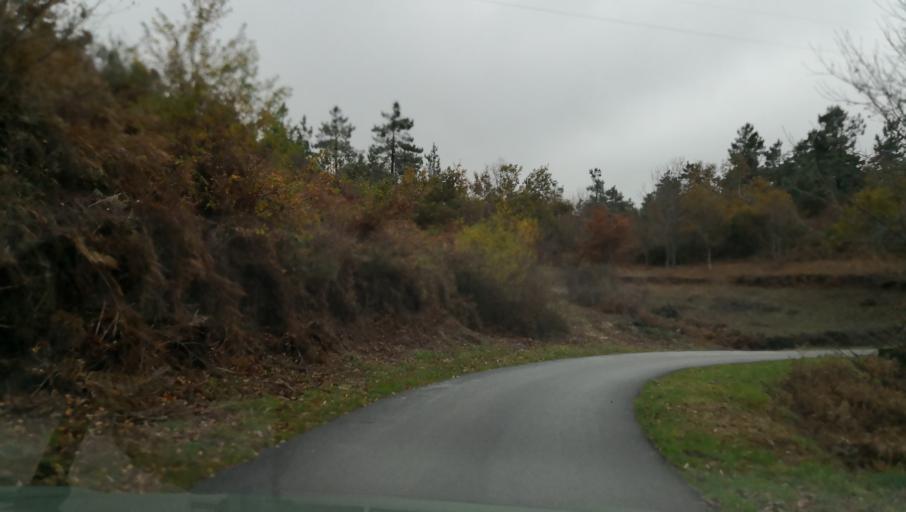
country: PT
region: Vila Real
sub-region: Mondim de Basto
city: Mondim de Basto
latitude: 41.3176
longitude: -7.8736
